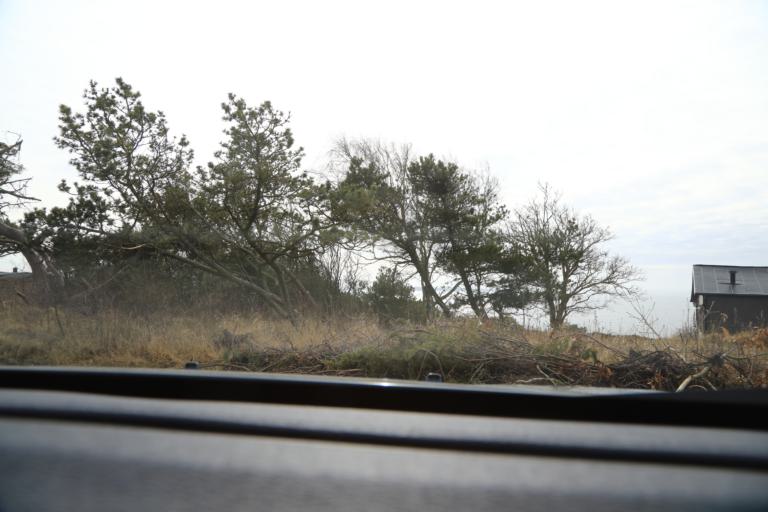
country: SE
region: Halland
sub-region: Kungsbacka Kommun
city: Frillesas
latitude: 57.2299
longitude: 12.1179
